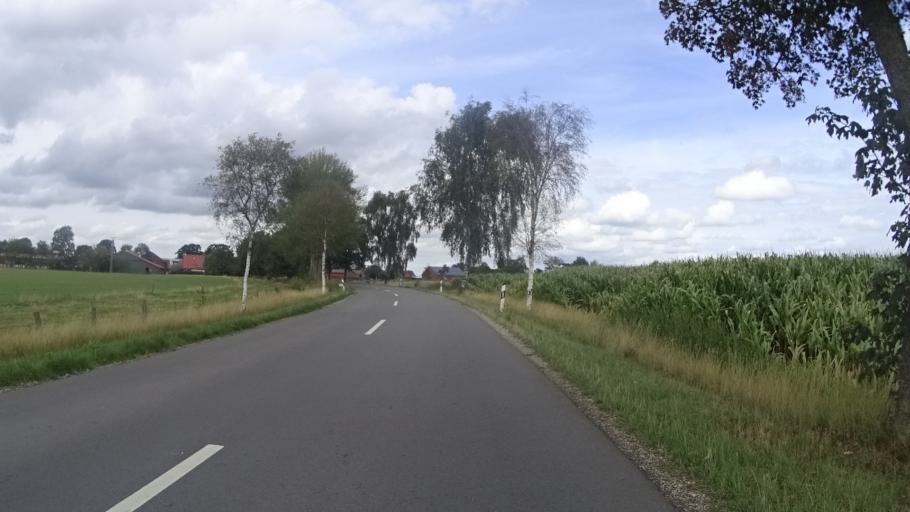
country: DE
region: Lower Saxony
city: Mittelstenahe
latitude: 53.6608
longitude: 9.0414
